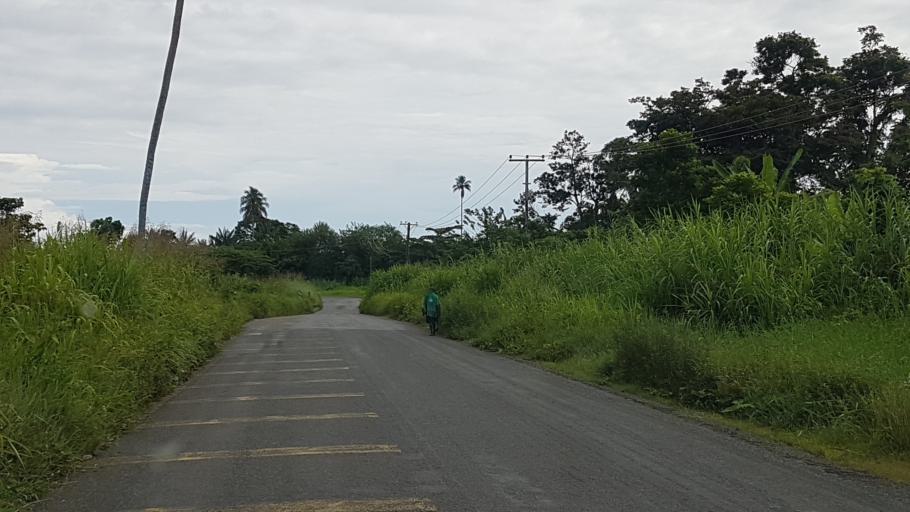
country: PG
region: Madang
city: Madang
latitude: -5.1087
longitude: 145.7912
